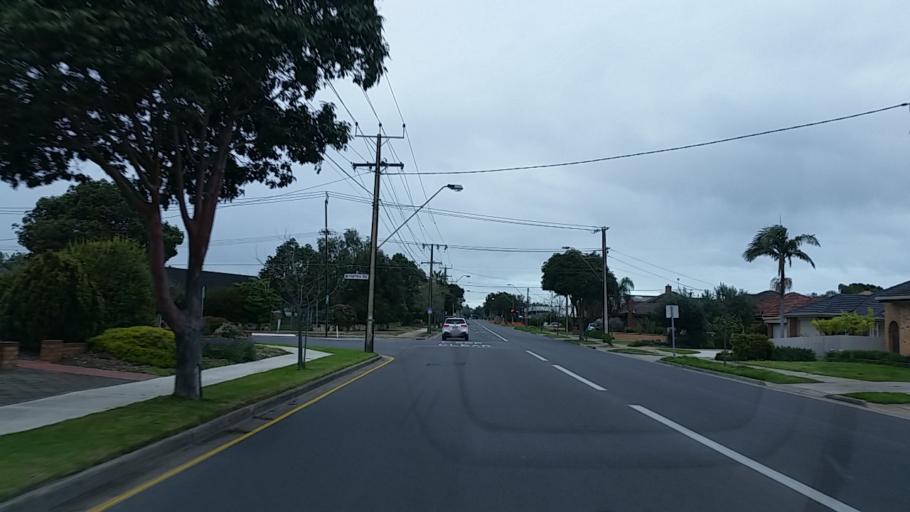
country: AU
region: South Australia
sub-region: Charles Sturt
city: Findon
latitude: -34.9120
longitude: 138.5339
